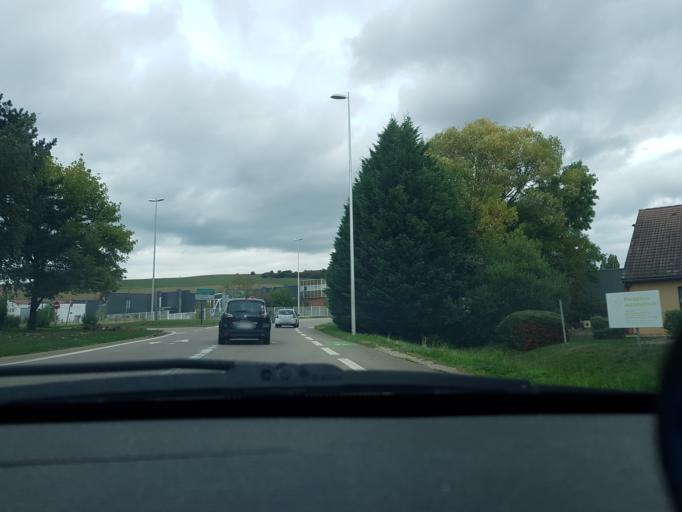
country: FR
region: Lorraine
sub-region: Departement de Meurthe-et-Moselle
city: Pulnoy
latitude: 48.7121
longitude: 6.2483
